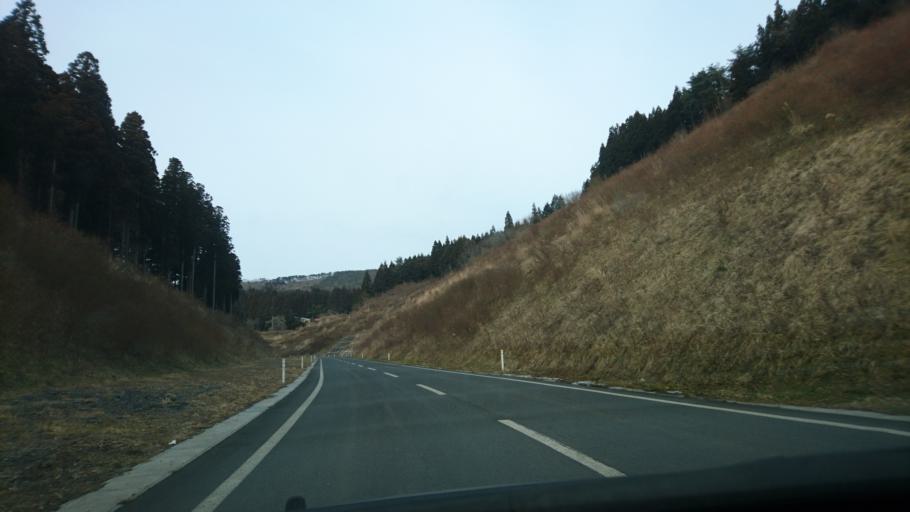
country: JP
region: Iwate
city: Ichinoseki
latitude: 38.8531
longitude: 141.3920
